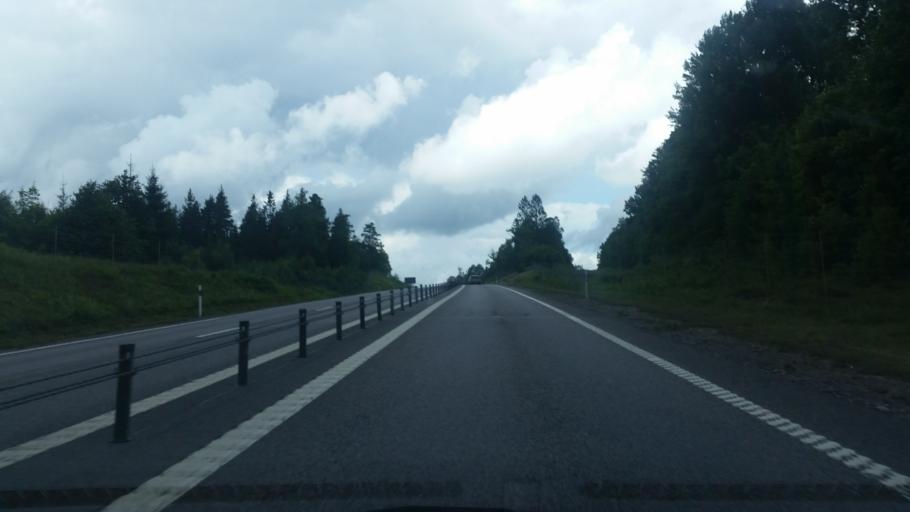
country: SE
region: Vaestra Goetaland
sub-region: Boras Kommun
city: Dalsjofors
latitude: 57.6446
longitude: 13.0683
